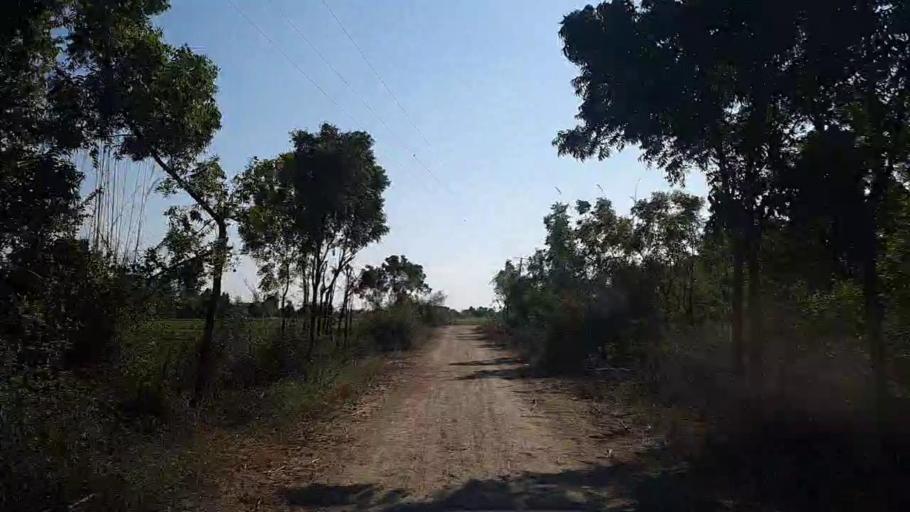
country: PK
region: Sindh
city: Khadro
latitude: 26.2721
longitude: 68.8157
